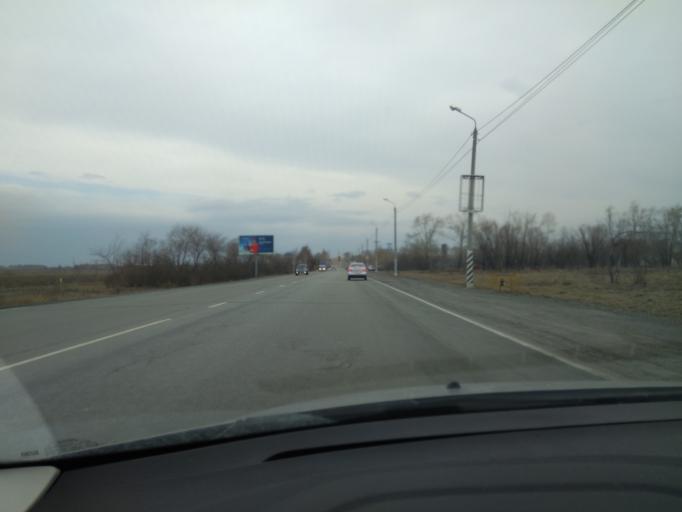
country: RU
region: Chelyabinsk
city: Potanino
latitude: 55.2896
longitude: 61.5106
